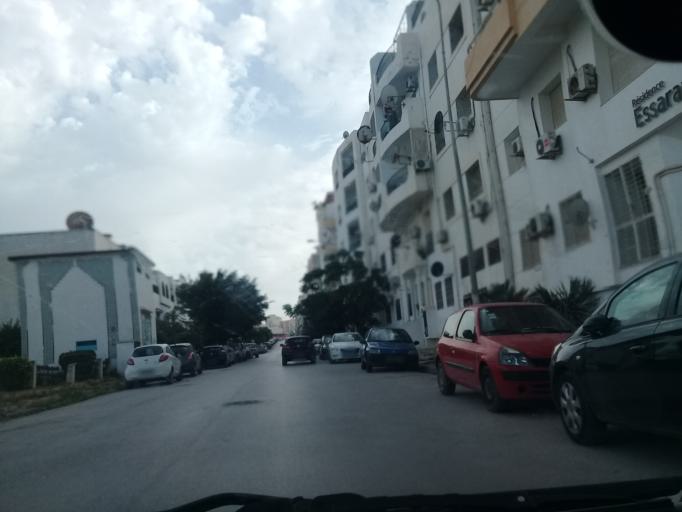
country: TN
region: Ariana
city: Ariana
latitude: 36.8647
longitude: 10.1686
